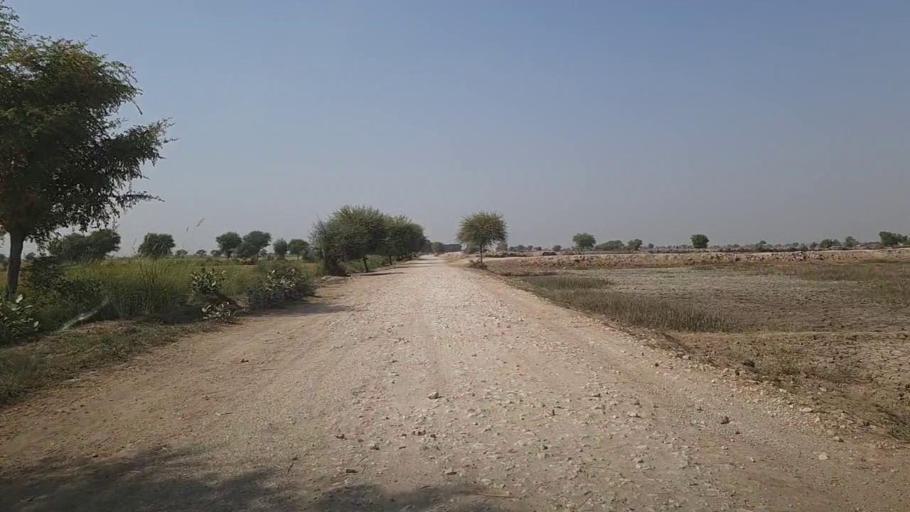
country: PK
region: Sindh
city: Kandhkot
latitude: 28.3931
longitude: 69.3016
